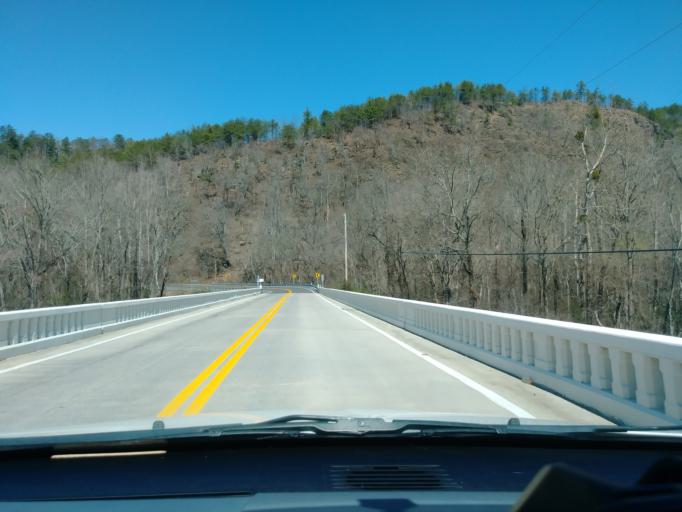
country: US
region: Tennessee
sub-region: Cocke County
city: Newport
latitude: 35.9209
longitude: -82.9592
